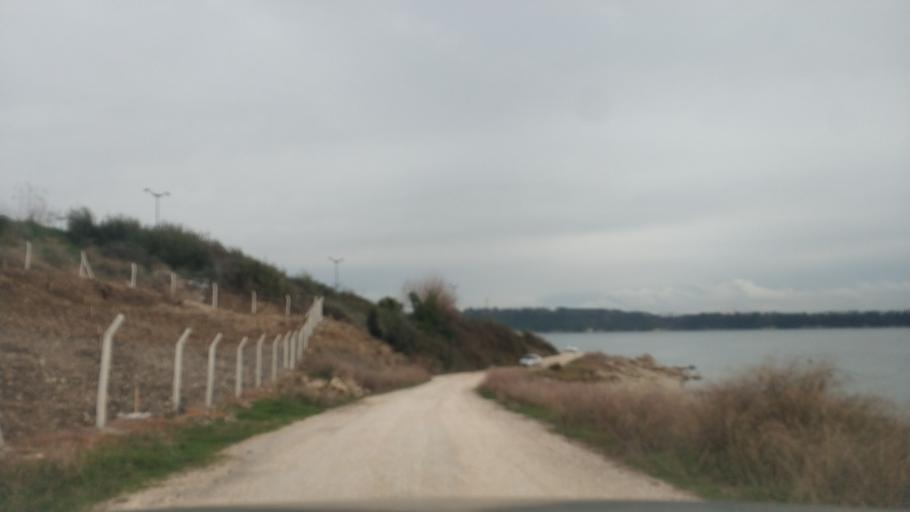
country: TR
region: Adana
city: Adana
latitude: 37.0781
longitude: 35.3294
